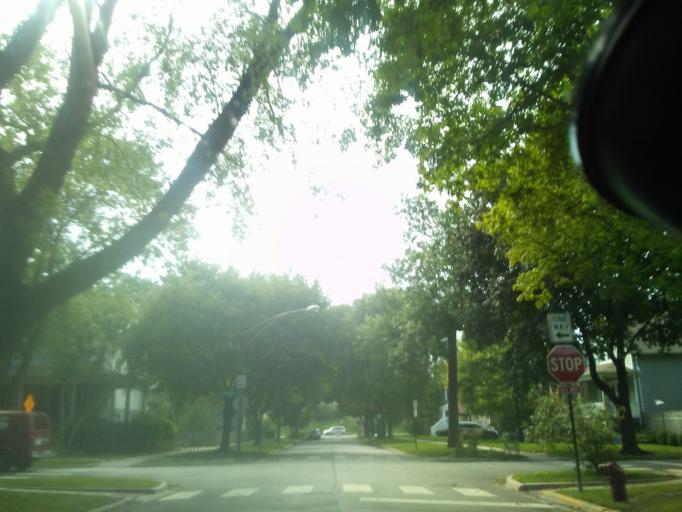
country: US
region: Illinois
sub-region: Cook County
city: Lincolnwood
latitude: 41.9779
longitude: -87.7535
